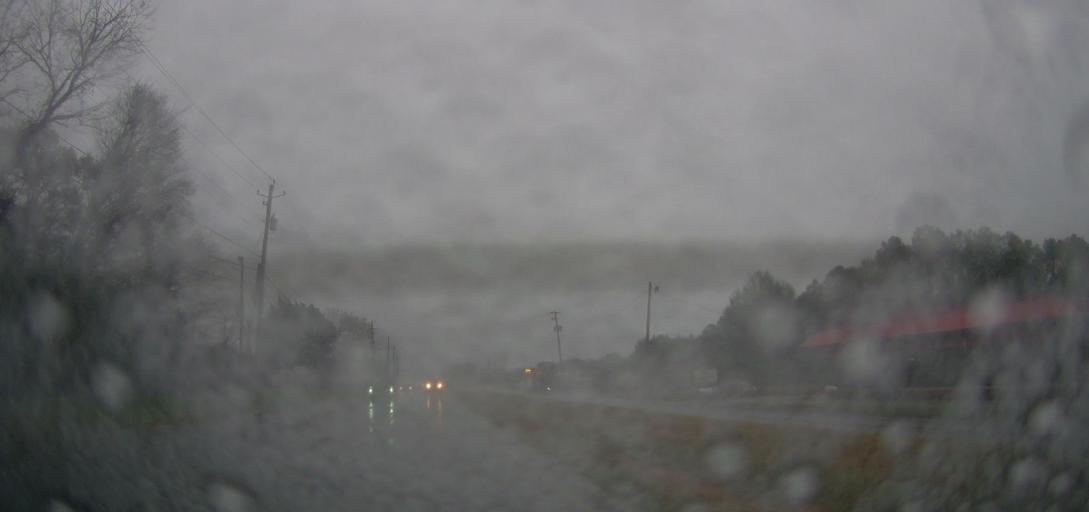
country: US
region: Alabama
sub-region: Autauga County
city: Prattville
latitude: 32.4015
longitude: -86.4013
